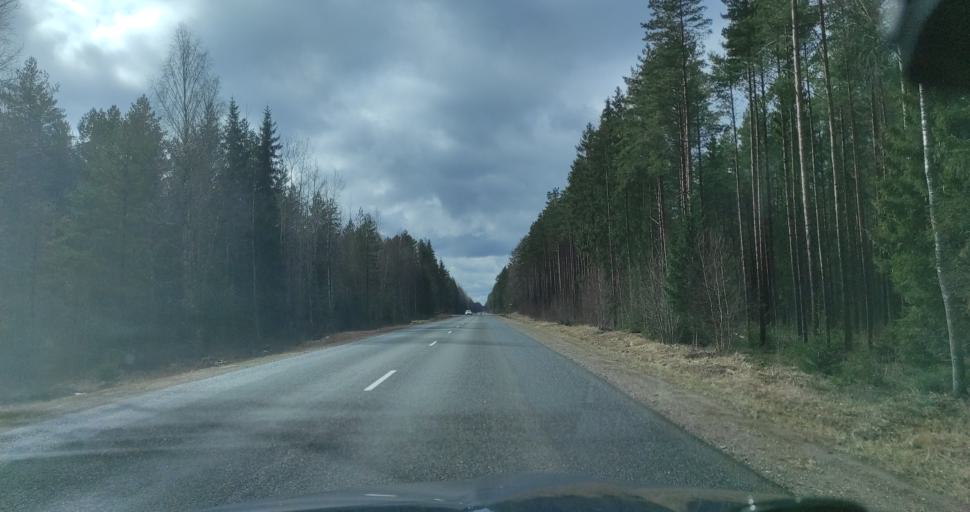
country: LV
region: Talsu Rajons
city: Stende
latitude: 57.1206
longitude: 22.5218
